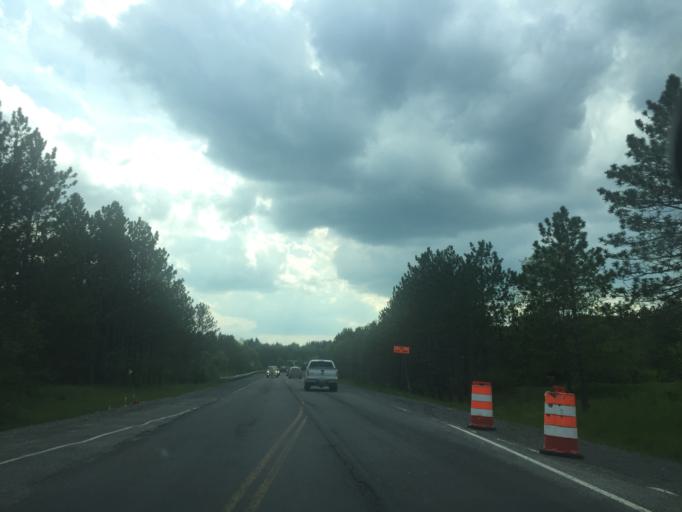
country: US
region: West Virginia
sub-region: Tucker County
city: Parsons
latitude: 39.1380
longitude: -79.4615
